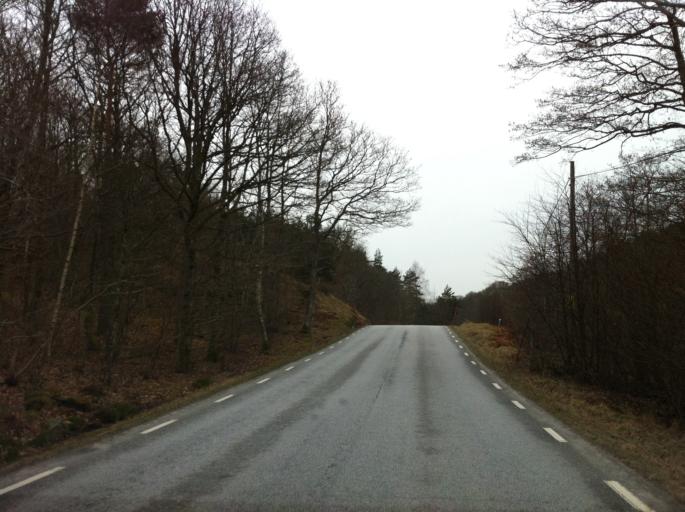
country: SE
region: Vaestra Goetaland
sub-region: Orust
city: Henan
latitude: 58.2650
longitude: 11.6842
